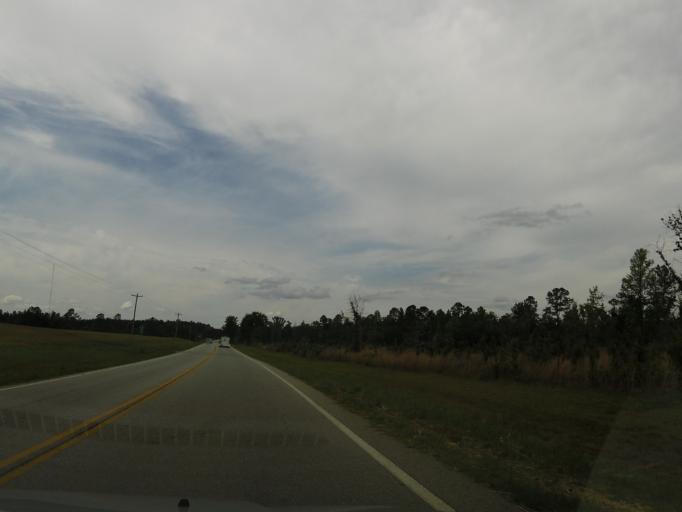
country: US
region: Georgia
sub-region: Emanuel County
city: Twin City
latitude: 32.4924
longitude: -82.2479
